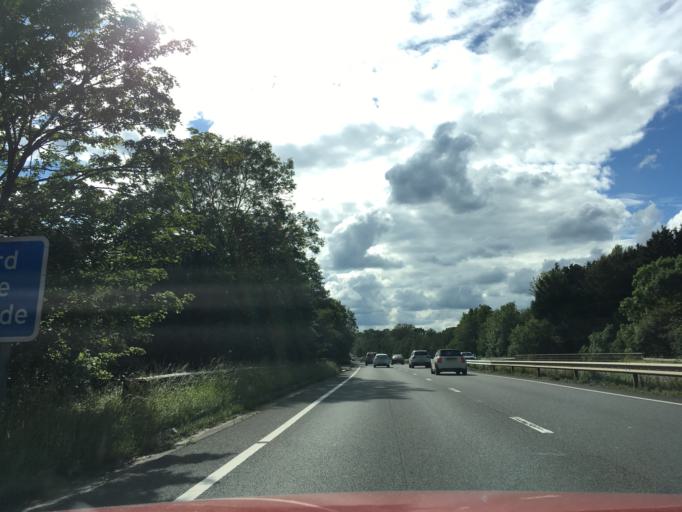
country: GB
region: England
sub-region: Oxfordshire
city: Wheatley
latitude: 51.7472
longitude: -1.1231
